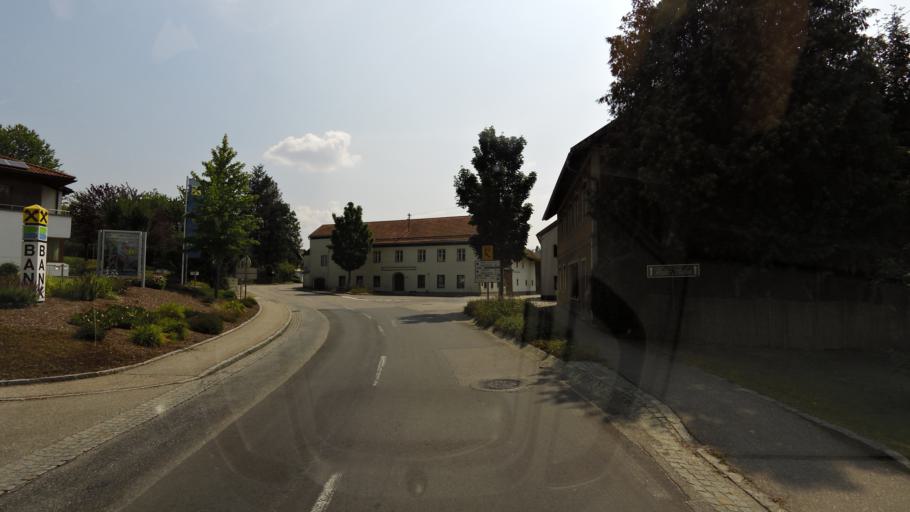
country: AT
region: Upper Austria
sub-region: Politischer Bezirk Braunau am Inn
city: Altheim
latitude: 48.2401
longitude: 13.3455
